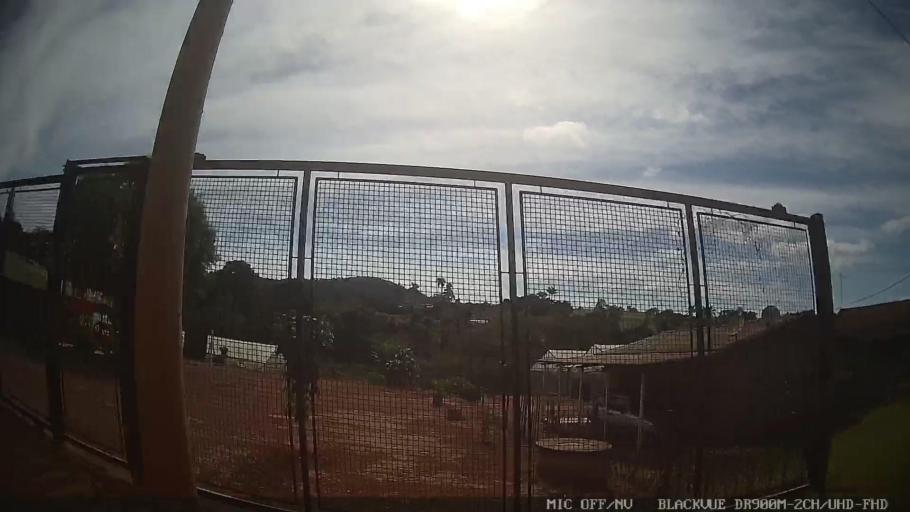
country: BR
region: Sao Paulo
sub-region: Jarinu
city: Jarinu
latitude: -23.0284
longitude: -46.6387
